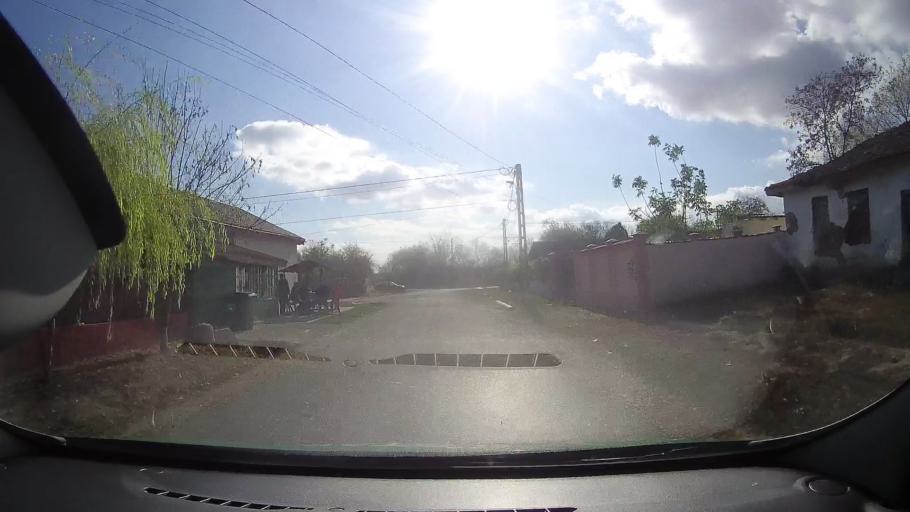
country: RO
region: Constanta
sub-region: Comuna Istria
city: Istria
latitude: 44.5724
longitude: 28.7148
